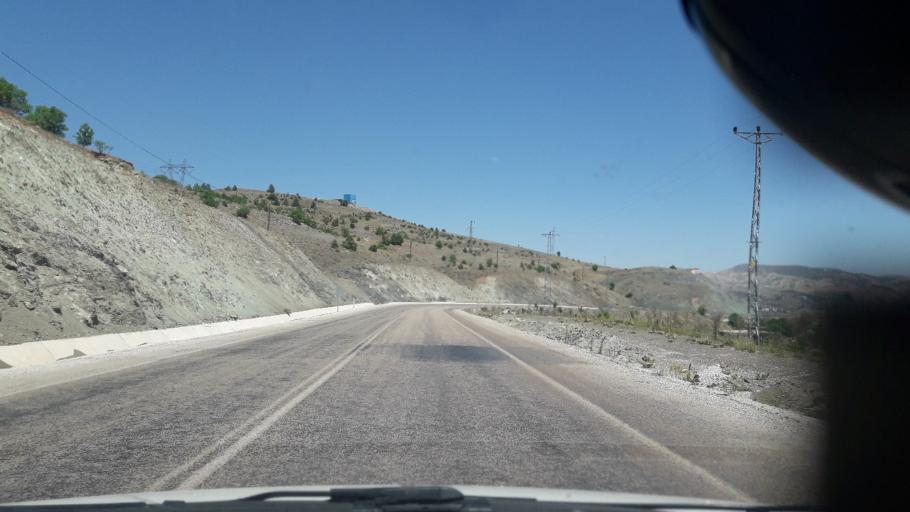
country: TR
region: Malatya
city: Hekimhan
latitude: 38.8217
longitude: 37.8754
